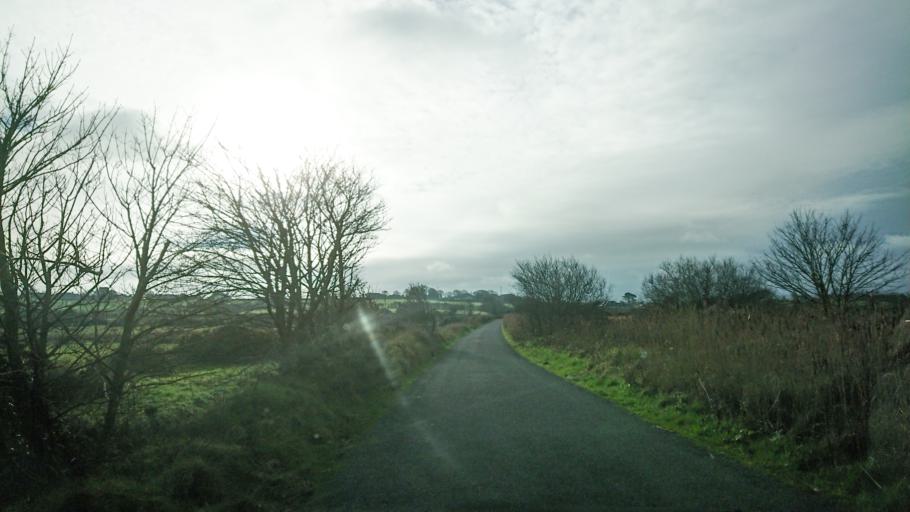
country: IE
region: Munster
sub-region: Waterford
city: Tra Mhor
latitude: 52.1609
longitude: -7.1880
